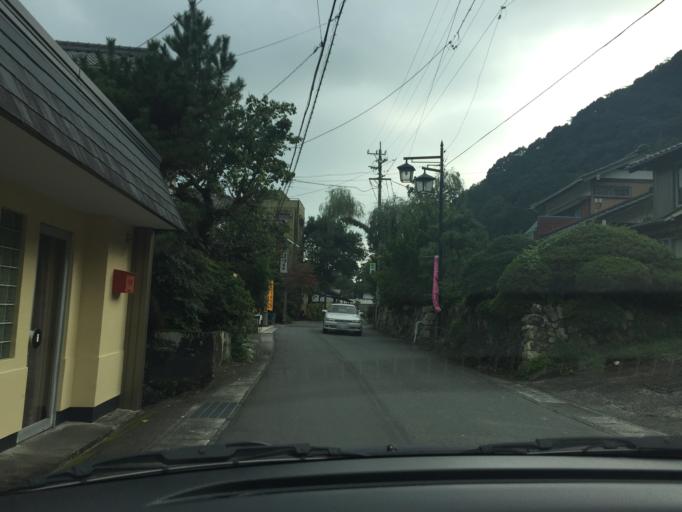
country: JP
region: Aichi
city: Shinshiro
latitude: 34.9707
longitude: 137.6138
